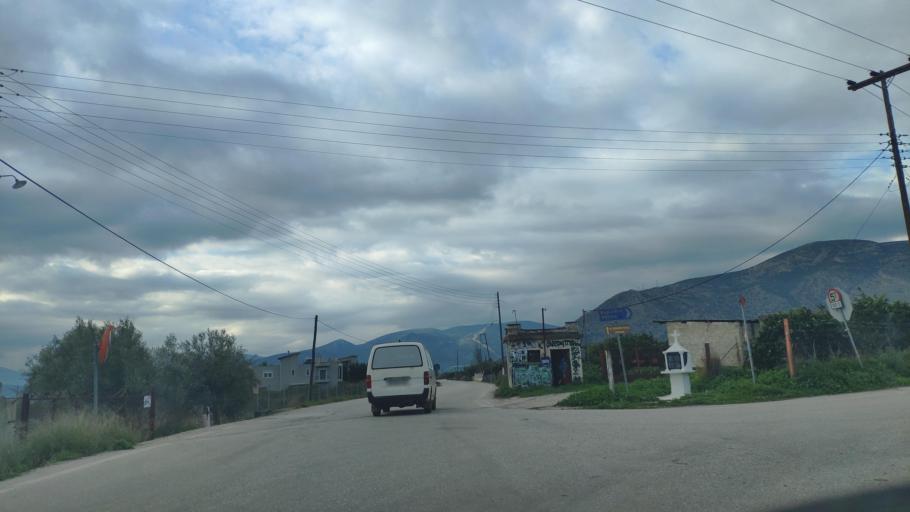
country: GR
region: Peloponnese
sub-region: Nomos Argolidos
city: Argos
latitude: 37.6152
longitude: 22.7080
